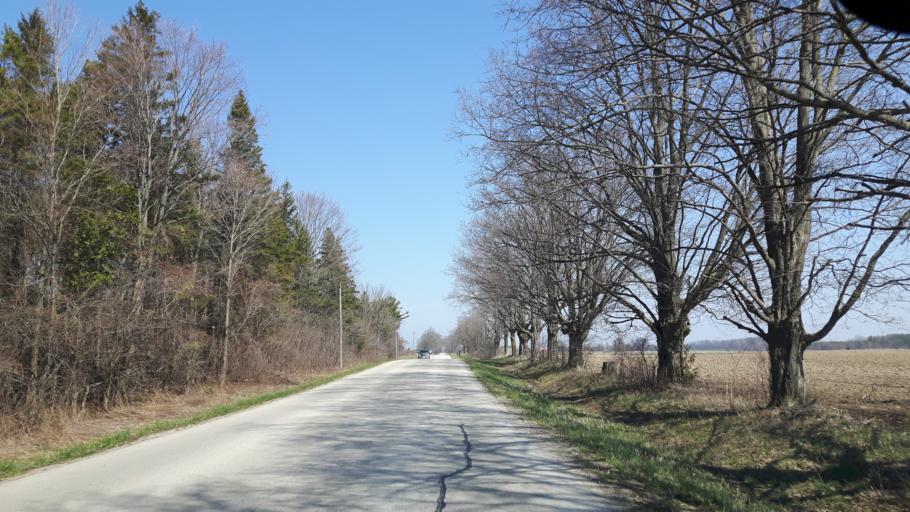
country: CA
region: Ontario
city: Goderich
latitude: 43.6328
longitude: -81.6846
